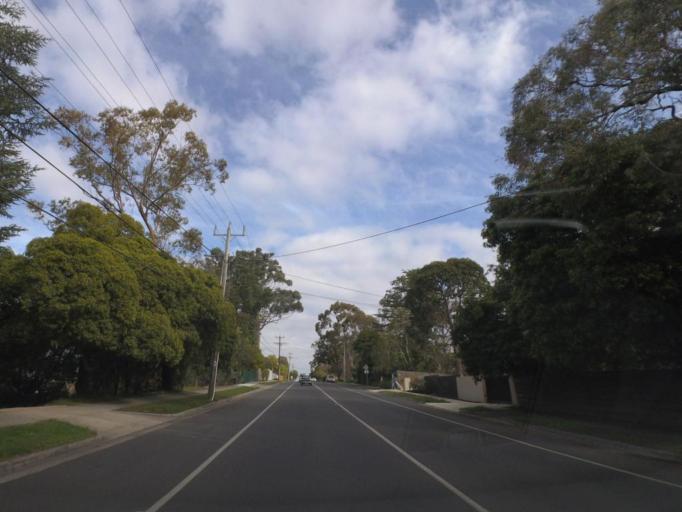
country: AU
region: Victoria
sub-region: Maroondah
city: Ringwood East
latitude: -37.7969
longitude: 145.2379
